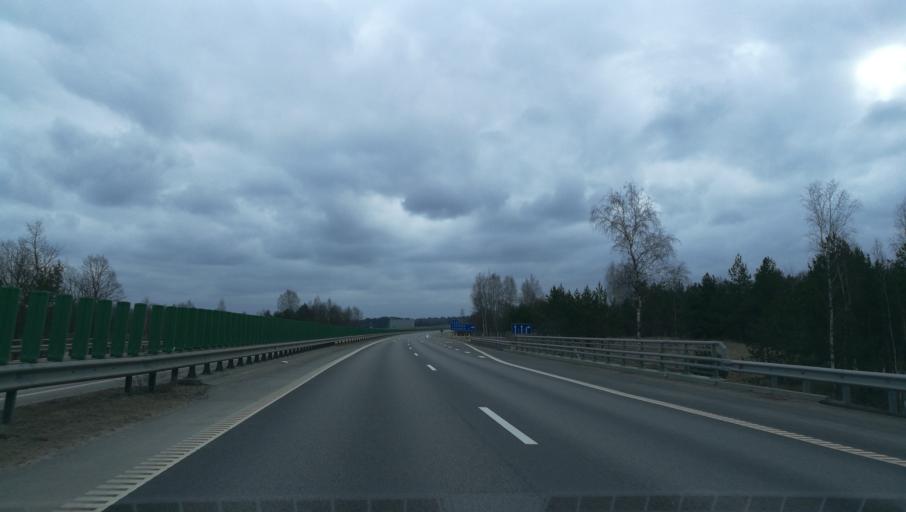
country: LT
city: Trakai
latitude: 54.7439
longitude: 24.9415
